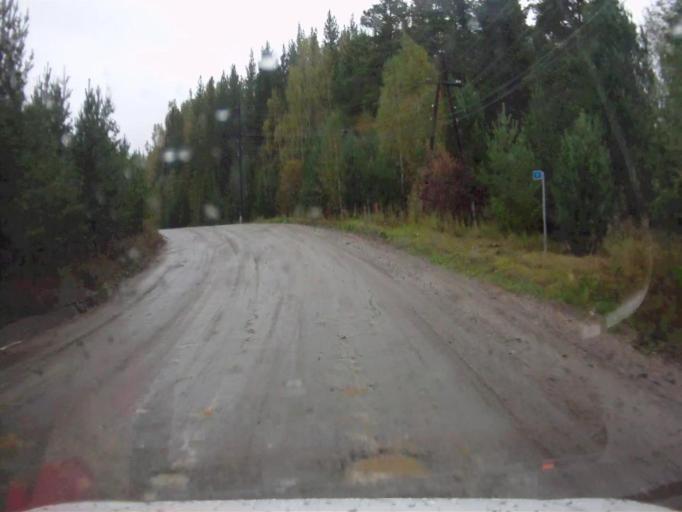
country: RU
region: Chelyabinsk
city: Kyshtym
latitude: 55.7462
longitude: 60.4915
